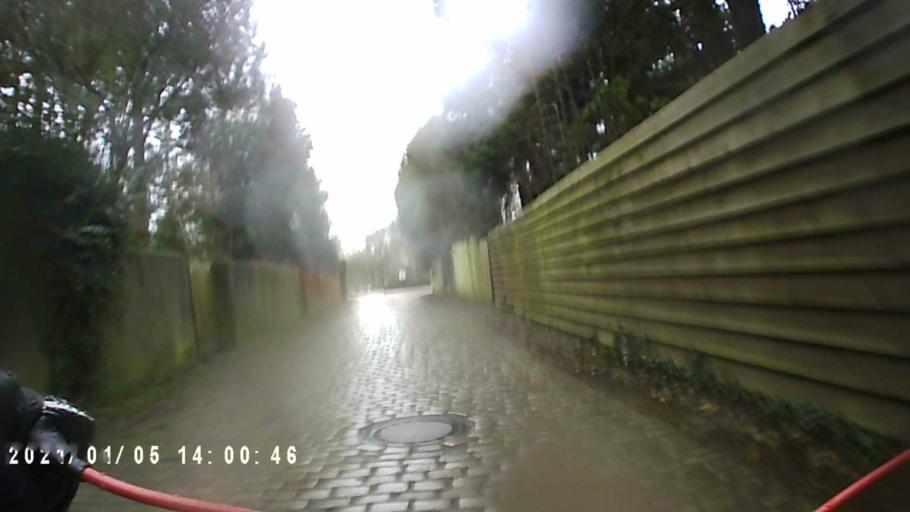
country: DE
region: Lower Saxony
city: Weener
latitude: 53.1673
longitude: 7.3574
